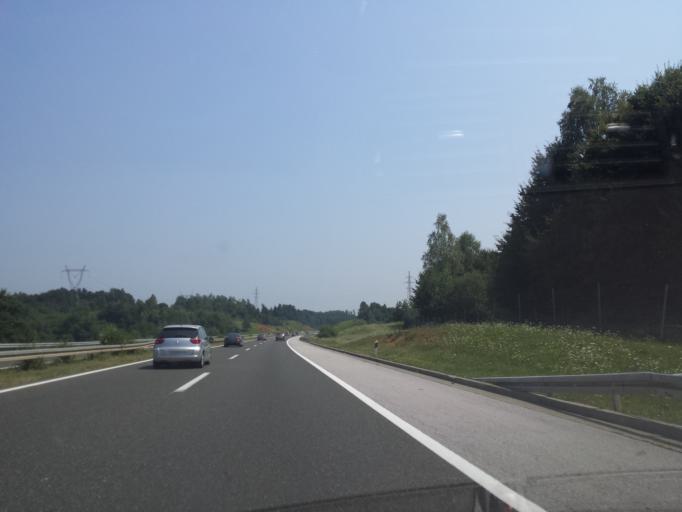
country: SI
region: Crnomelj
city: Crnomelj
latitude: 45.4404
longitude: 15.3383
